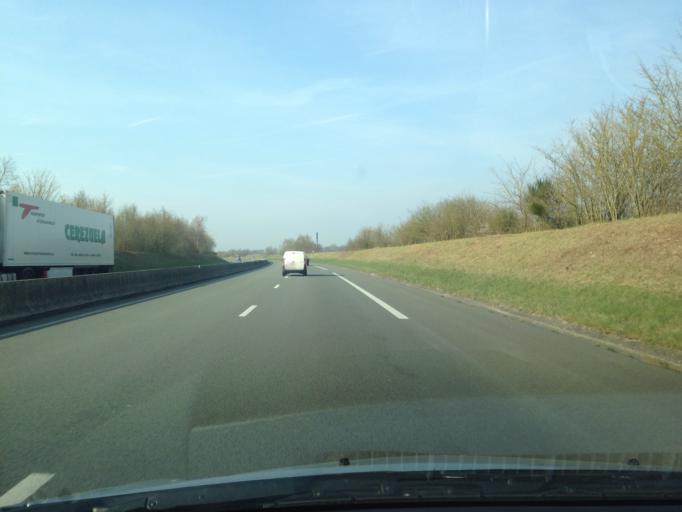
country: FR
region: Nord-Pas-de-Calais
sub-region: Departement du Pas-de-Calais
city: Saint-Josse
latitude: 50.4659
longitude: 1.7034
